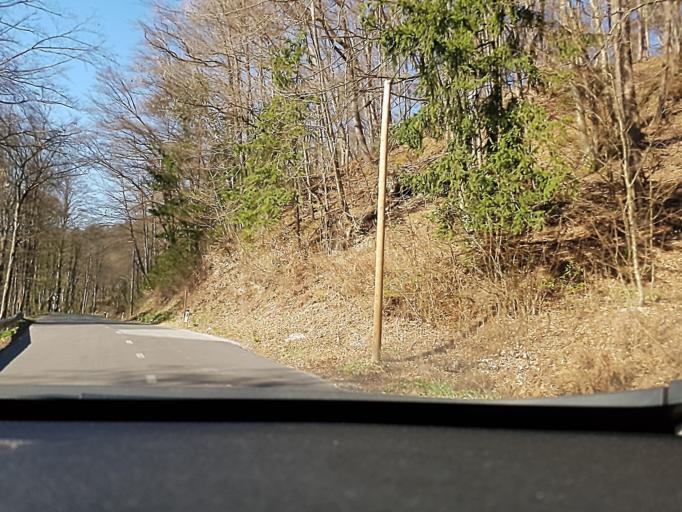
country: SI
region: Trzin
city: Trzin
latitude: 46.1102
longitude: 14.5127
